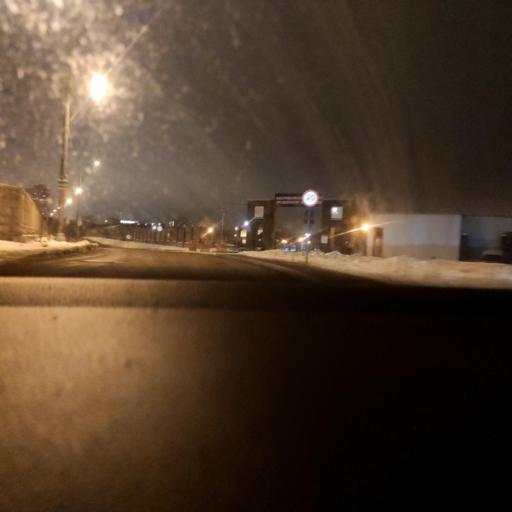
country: RU
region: Moskovskaya
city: Vostryakovo
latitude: 55.6597
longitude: 37.4528
